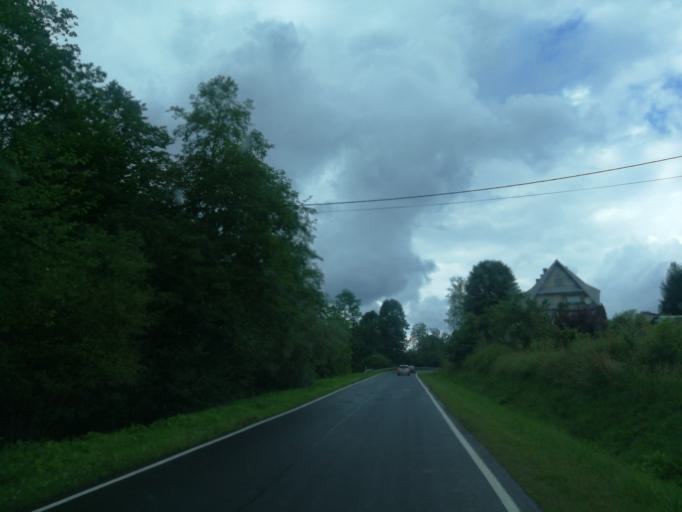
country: PL
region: Subcarpathian Voivodeship
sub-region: Powiat leski
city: Olszanica
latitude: 49.4321
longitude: 22.4559
